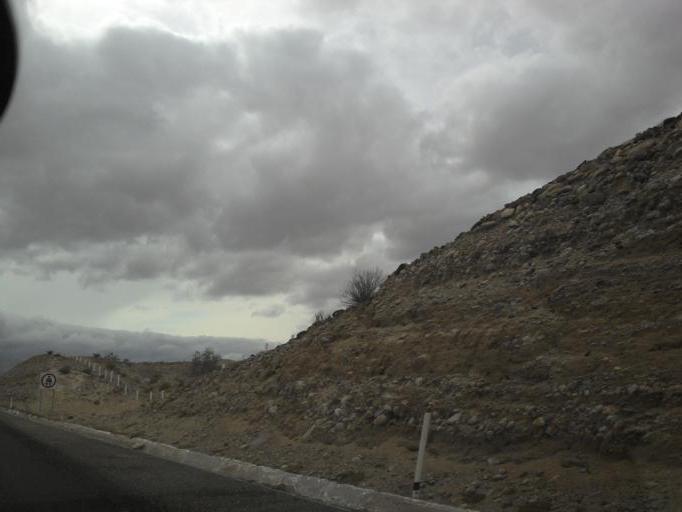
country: MX
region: Baja California
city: Progreso
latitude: 32.5644
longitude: -115.8699
